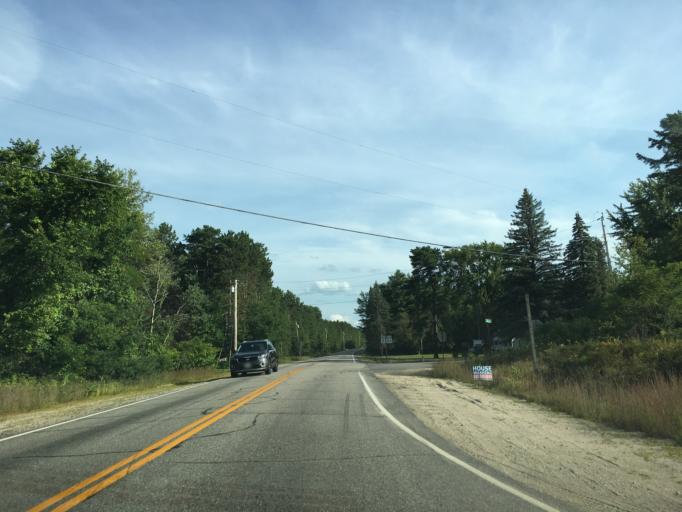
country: US
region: Maine
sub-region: Oxford County
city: Brownfield
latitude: 43.9449
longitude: -70.8886
